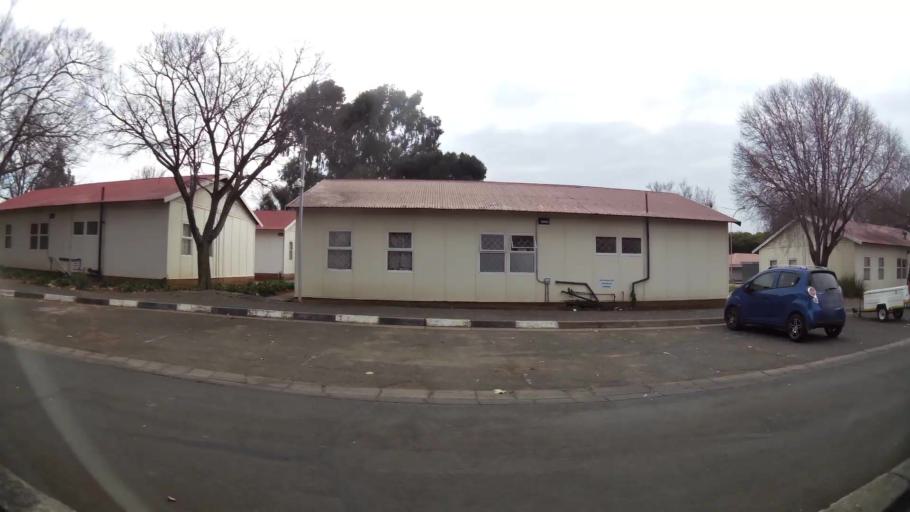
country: ZA
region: Orange Free State
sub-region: Mangaung Metropolitan Municipality
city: Bloemfontein
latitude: -29.1140
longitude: 26.1868
